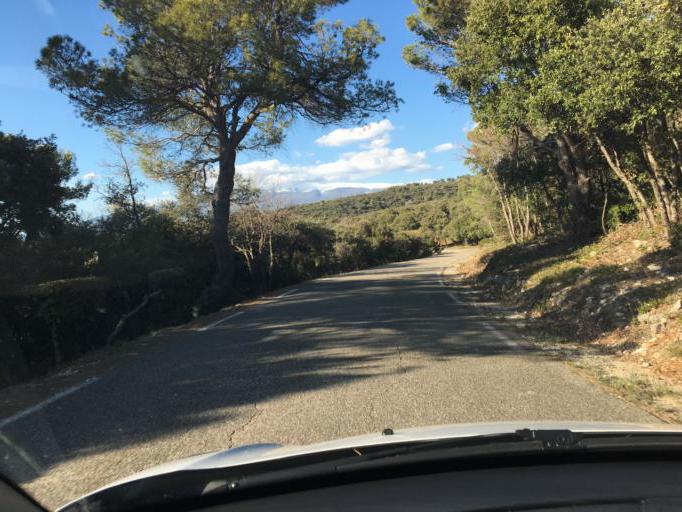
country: FR
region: Provence-Alpes-Cote d'Azur
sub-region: Departement du Vaucluse
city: Villes-sur-Auzon
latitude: 44.0409
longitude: 5.2556
